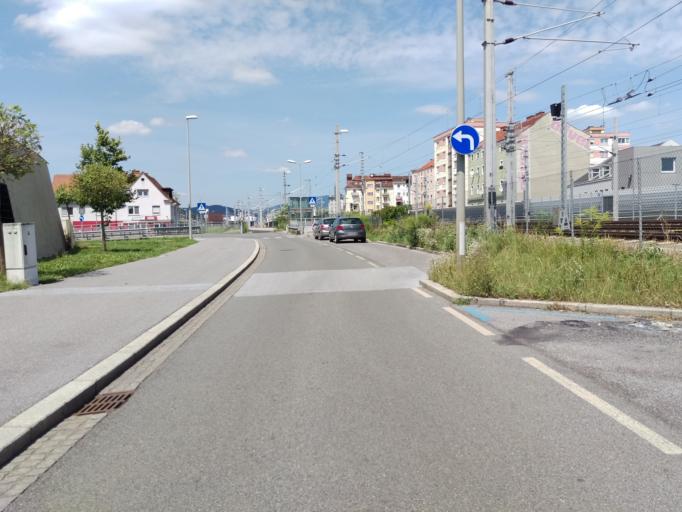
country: AT
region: Styria
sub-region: Graz Stadt
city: Wetzelsdorf
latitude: 47.0672
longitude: 15.4185
